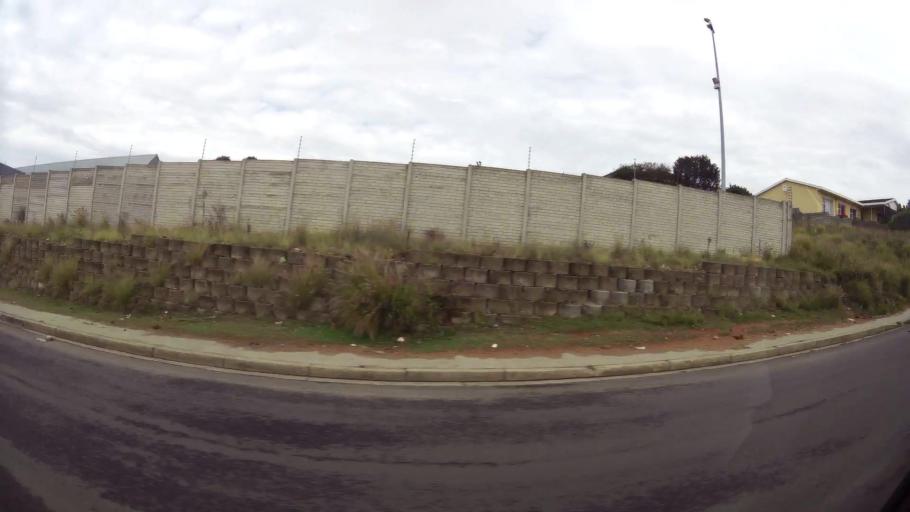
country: ZA
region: Eastern Cape
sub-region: Nelson Mandela Bay Metropolitan Municipality
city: Port Elizabeth
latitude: -33.9463
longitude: 25.5989
